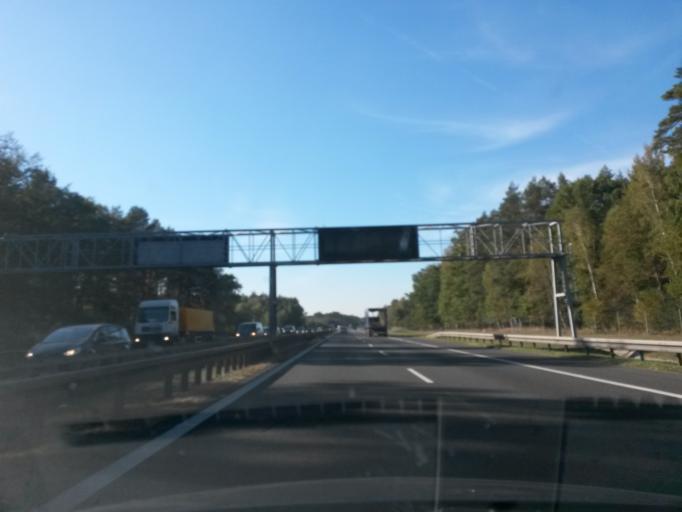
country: PL
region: Opole Voivodeship
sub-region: Powiat opolski
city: Dabrowa
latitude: 50.6651
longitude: 17.6850
